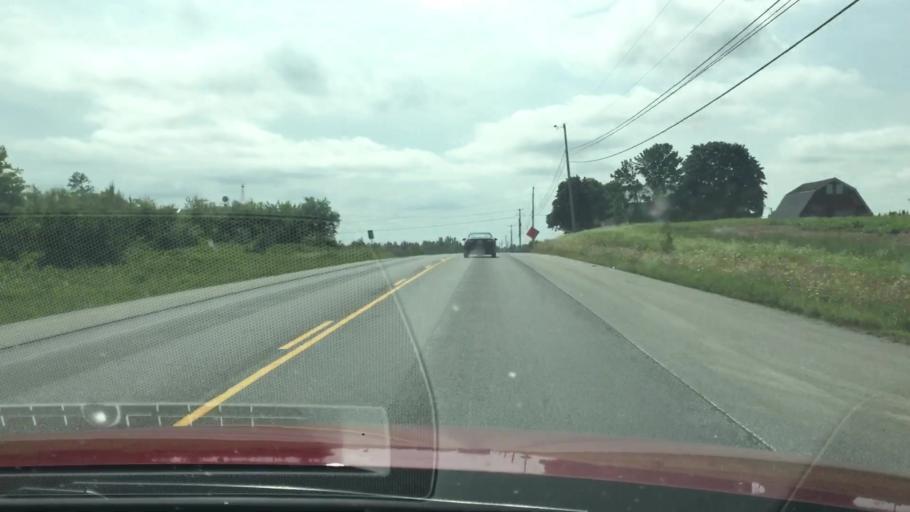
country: US
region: Maine
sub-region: Aroostook County
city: Houlton
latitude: 46.3419
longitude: -67.8419
